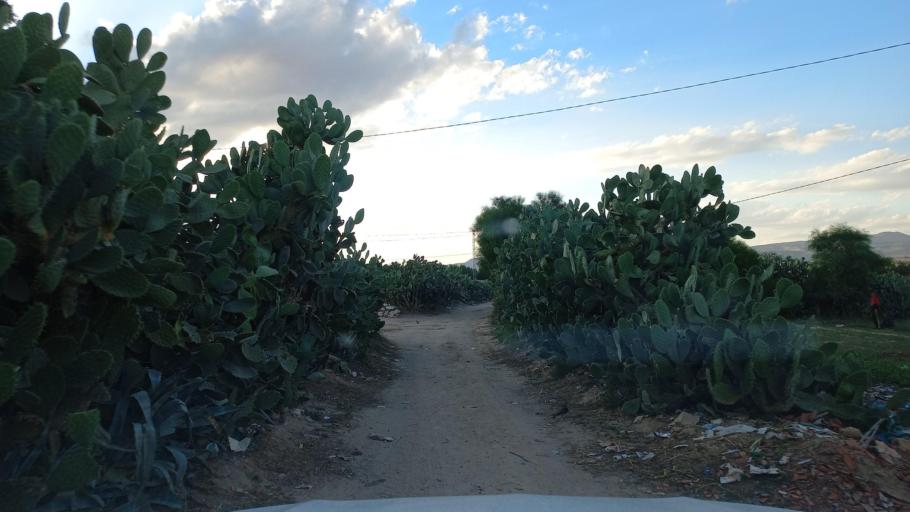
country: TN
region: Al Qasrayn
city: Sbiba
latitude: 35.3772
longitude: 9.0564
